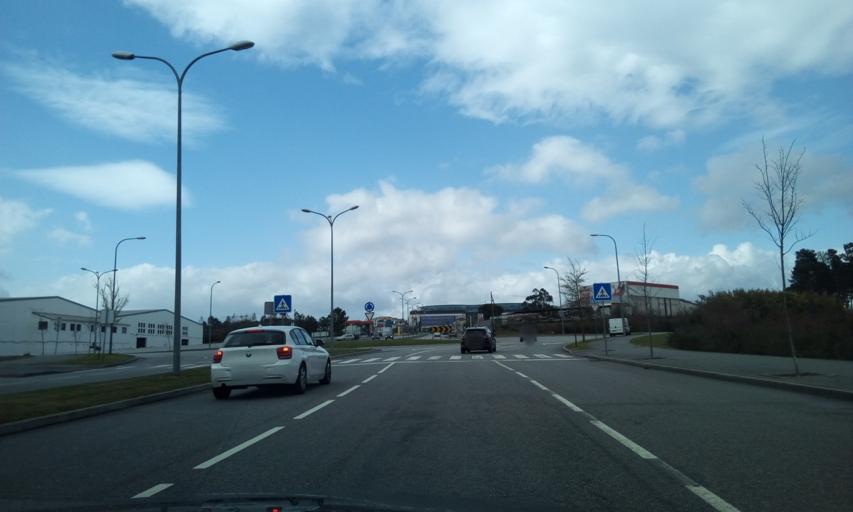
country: PT
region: Viseu
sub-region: Viseu
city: Viseu
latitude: 40.6357
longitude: -7.9072
